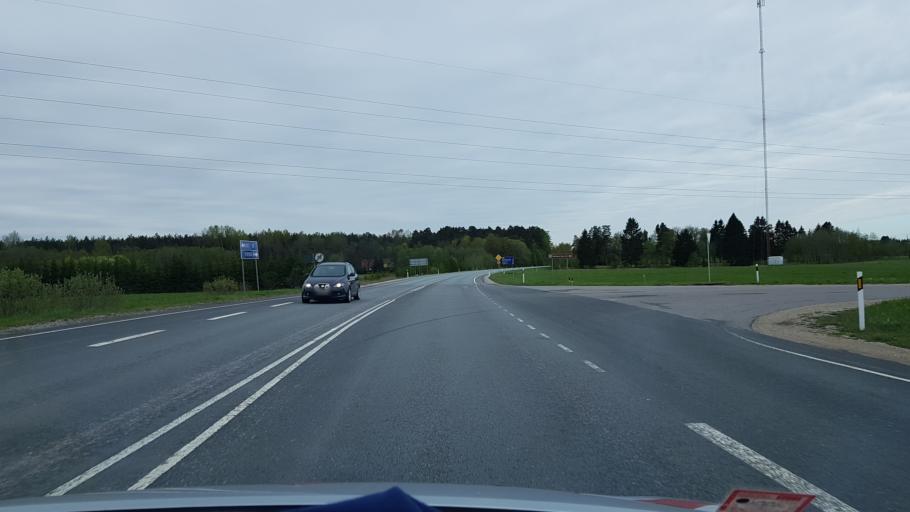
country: EE
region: Harju
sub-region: Nissi vald
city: Turba
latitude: 58.9023
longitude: 24.1093
